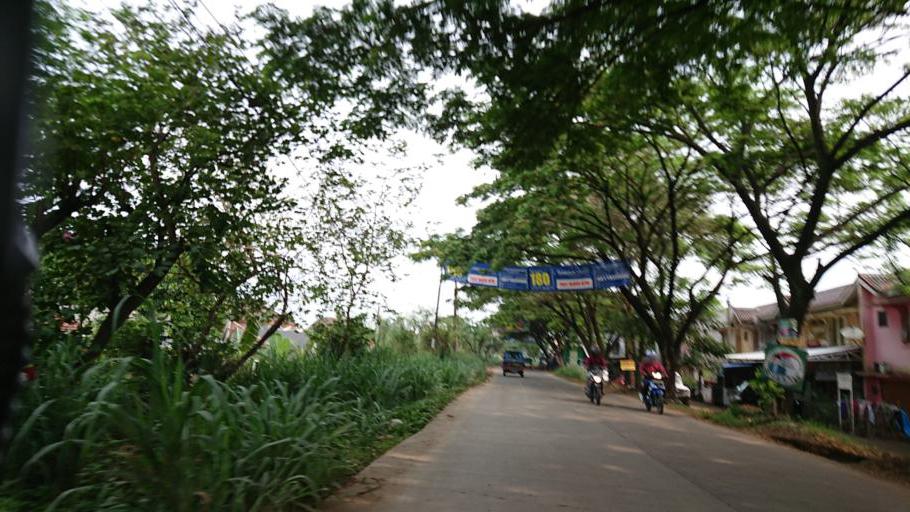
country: ID
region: West Java
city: Parung
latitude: -6.3871
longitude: 106.6818
